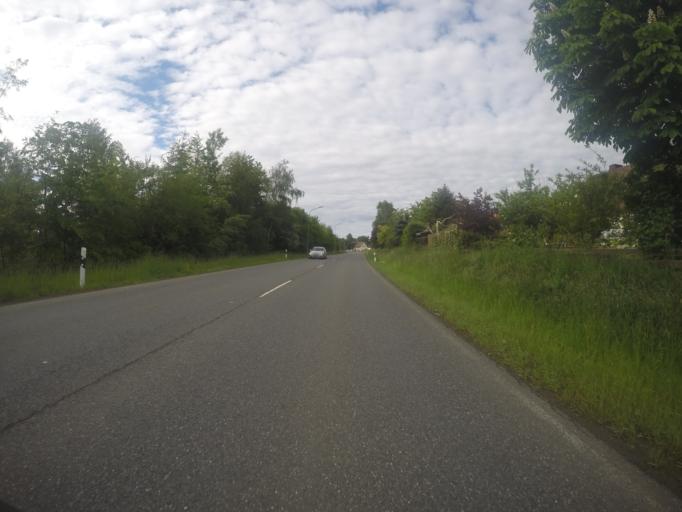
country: DE
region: Bavaria
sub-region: Upper Franconia
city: Schonwald
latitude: 50.2082
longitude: 12.0950
